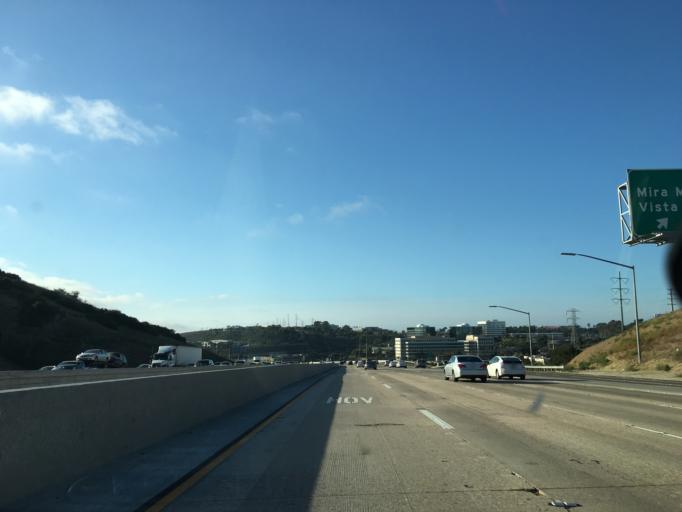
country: US
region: California
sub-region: San Diego County
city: La Jolla
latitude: 32.8842
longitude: -117.2021
